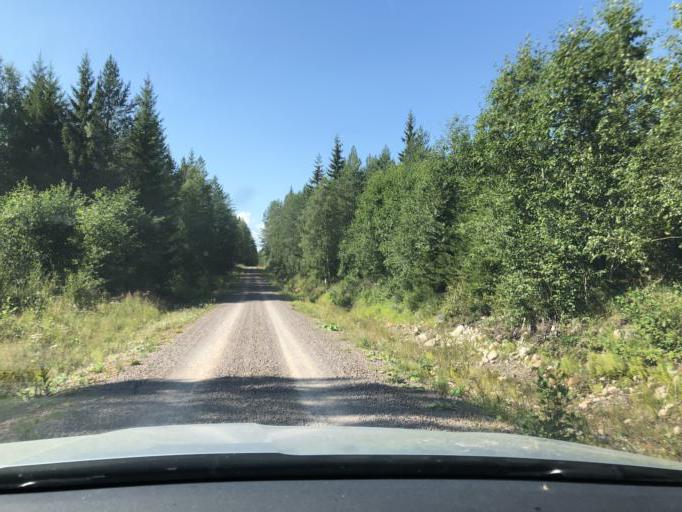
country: SE
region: Dalarna
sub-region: Orsa Kommun
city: Orsa
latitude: 61.2201
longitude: 14.7250
